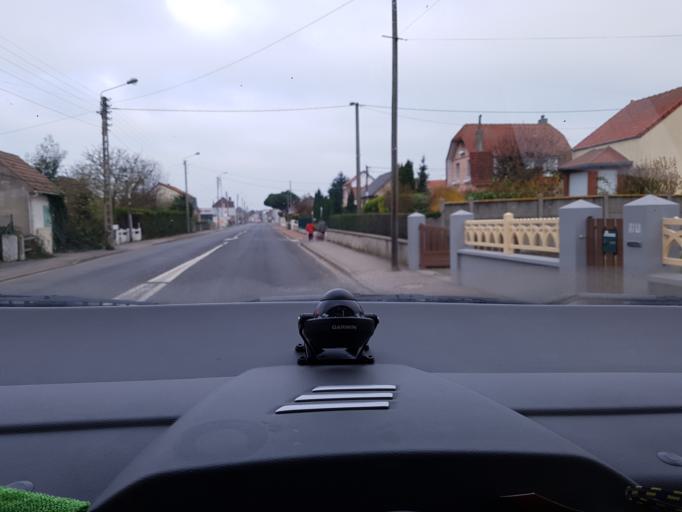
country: FR
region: Picardie
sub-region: Departement de la Somme
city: Mers-les-Bains
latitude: 50.0621
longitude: 1.4044
